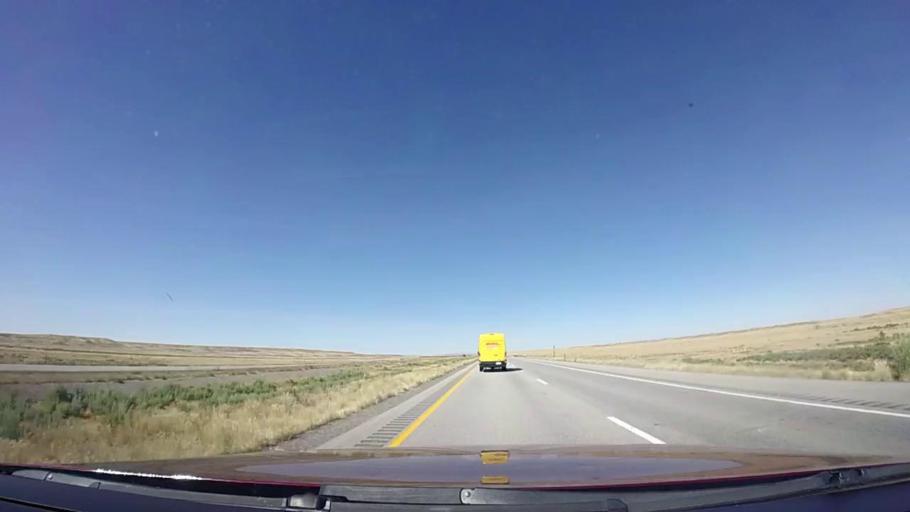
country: US
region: Wyoming
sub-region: Carbon County
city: Rawlins
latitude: 41.6613
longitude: -108.0633
